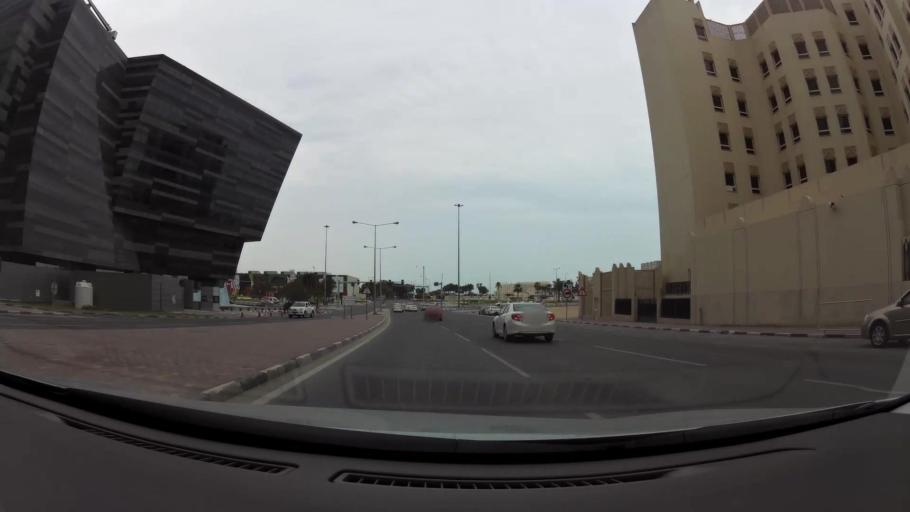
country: QA
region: Baladiyat ad Dawhah
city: Doha
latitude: 25.2903
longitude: 51.5441
